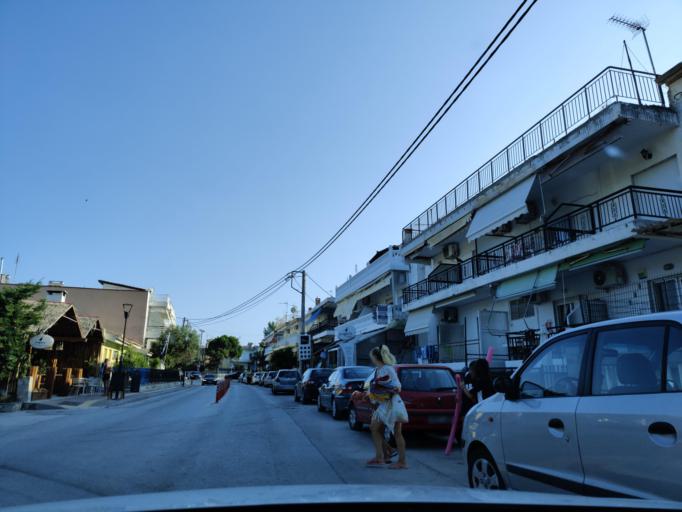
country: GR
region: East Macedonia and Thrace
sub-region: Nomos Kavalas
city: Nea Peramos
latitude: 40.8338
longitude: 24.3046
